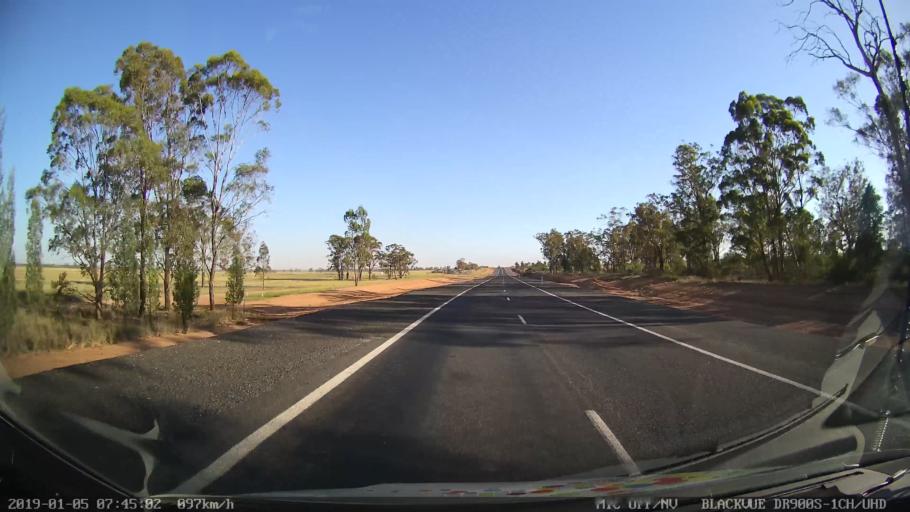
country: AU
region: New South Wales
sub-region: Gilgandra
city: Gilgandra
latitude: -31.8639
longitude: 148.6410
